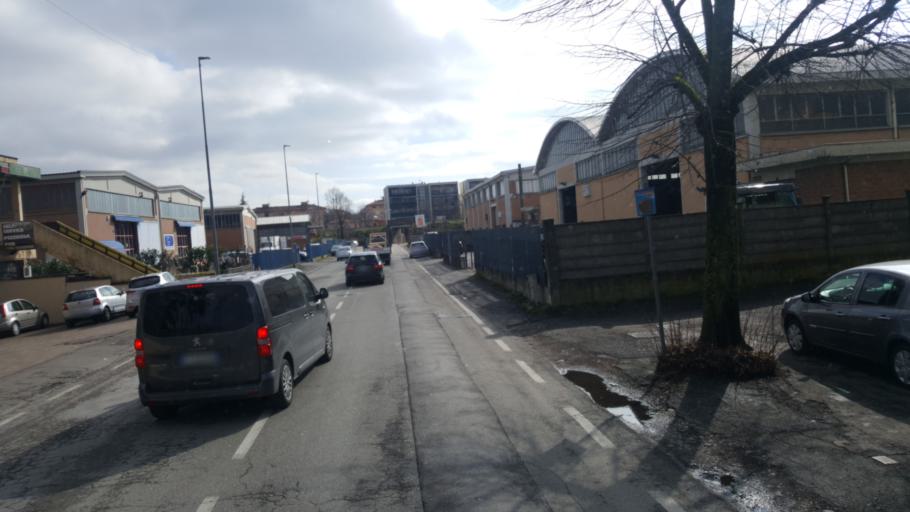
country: IT
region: Emilia-Romagna
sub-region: Provincia di Parma
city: Parma
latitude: 44.8105
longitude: 10.3040
